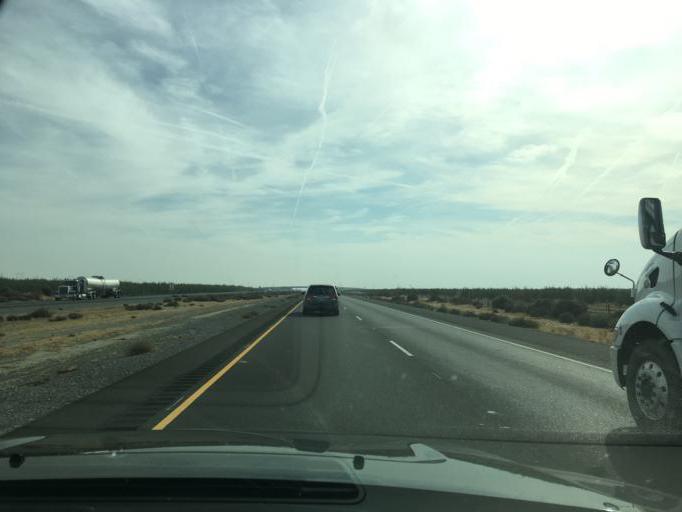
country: US
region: California
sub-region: Kings County
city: Kettleman City
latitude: 35.9414
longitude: -119.9193
